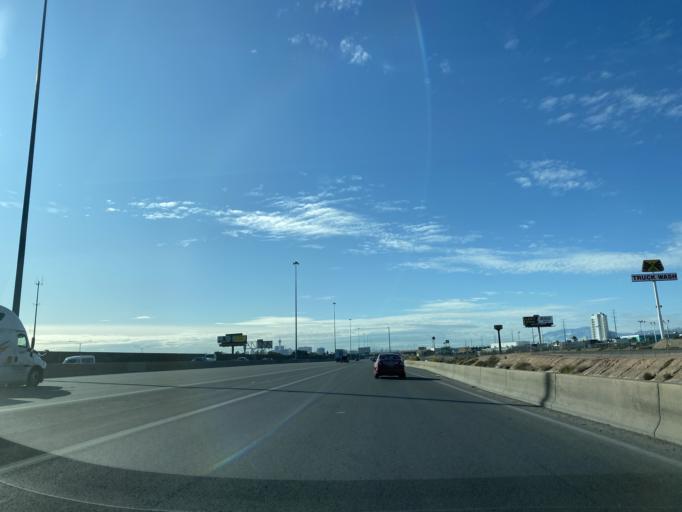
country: US
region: Nevada
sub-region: Clark County
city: North Las Vegas
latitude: 36.2147
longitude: -115.1266
